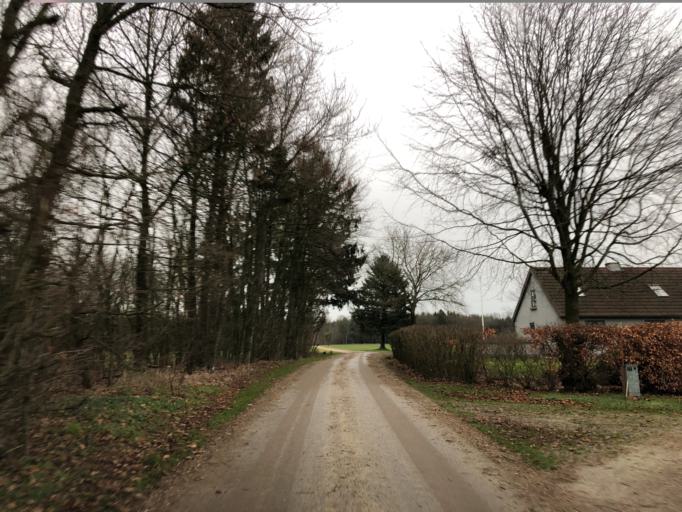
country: DK
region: Central Jutland
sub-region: Holstebro Kommune
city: Vinderup
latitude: 56.3772
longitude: 8.8640
